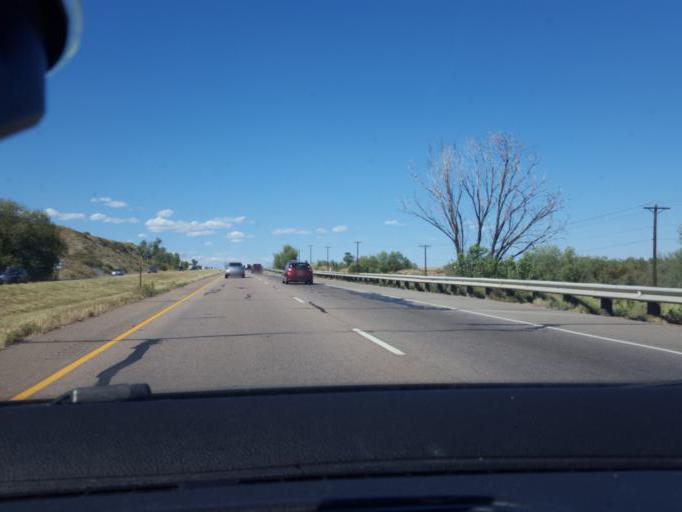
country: US
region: Colorado
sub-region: El Paso County
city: Fountain
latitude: 38.6839
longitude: -104.7156
